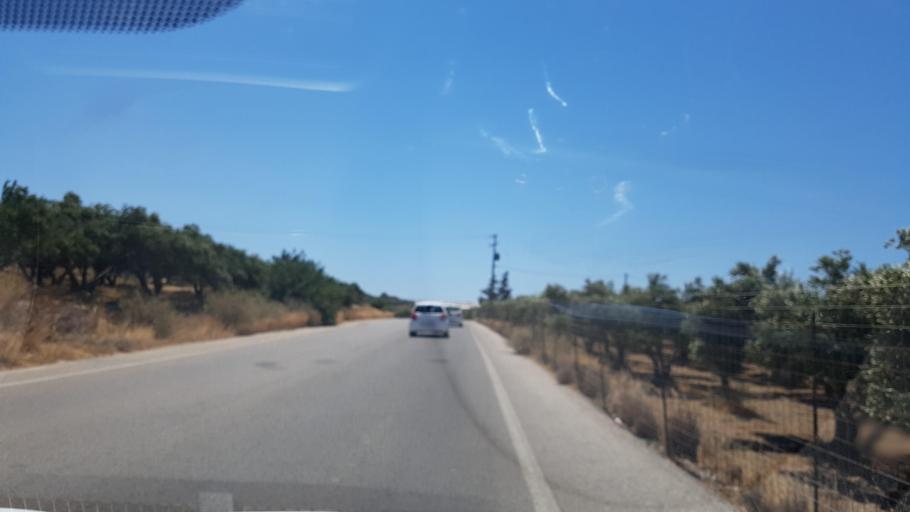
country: GR
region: Crete
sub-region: Nomos Chanias
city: Palaiochora
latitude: 35.3002
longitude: 23.5385
